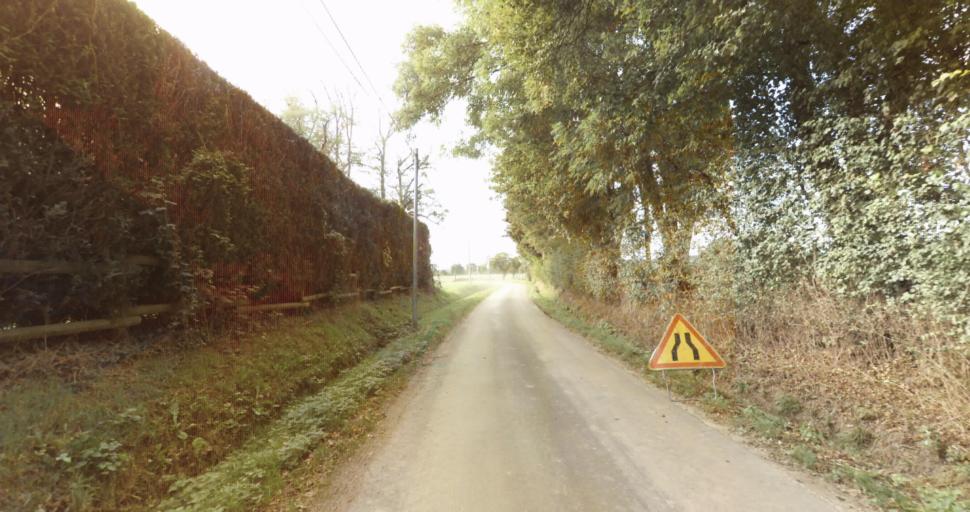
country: FR
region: Lower Normandy
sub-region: Departement de l'Orne
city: Gace
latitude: 48.7085
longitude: 0.2741
